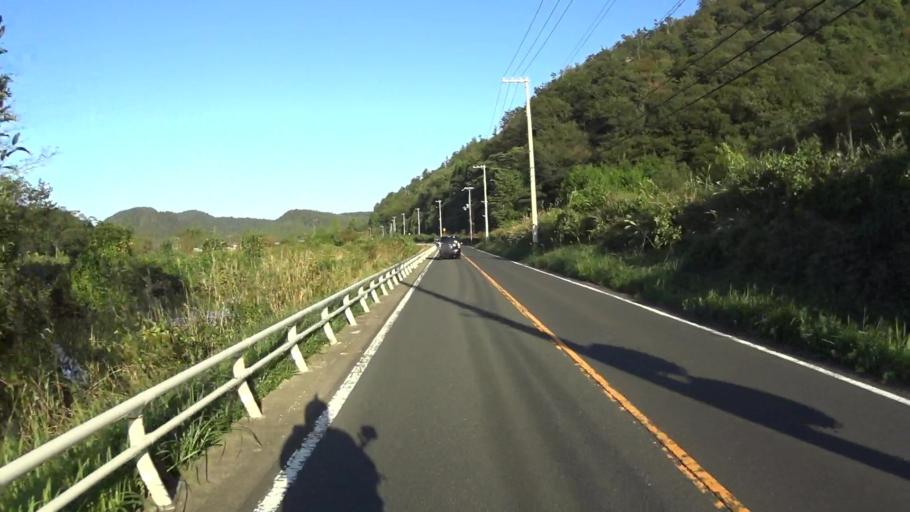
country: JP
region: Hyogo
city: Toyooka
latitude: 35.6052
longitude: 134.9124
